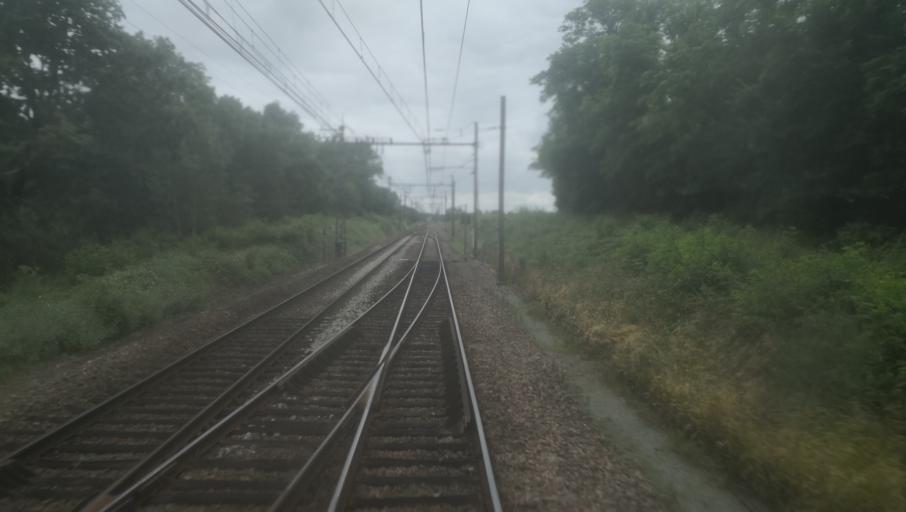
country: FR
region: Midi-Pyrenees
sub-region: Departement du Tarn-et-Garonne
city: Finhan
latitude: 43.9036
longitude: 1.2652
